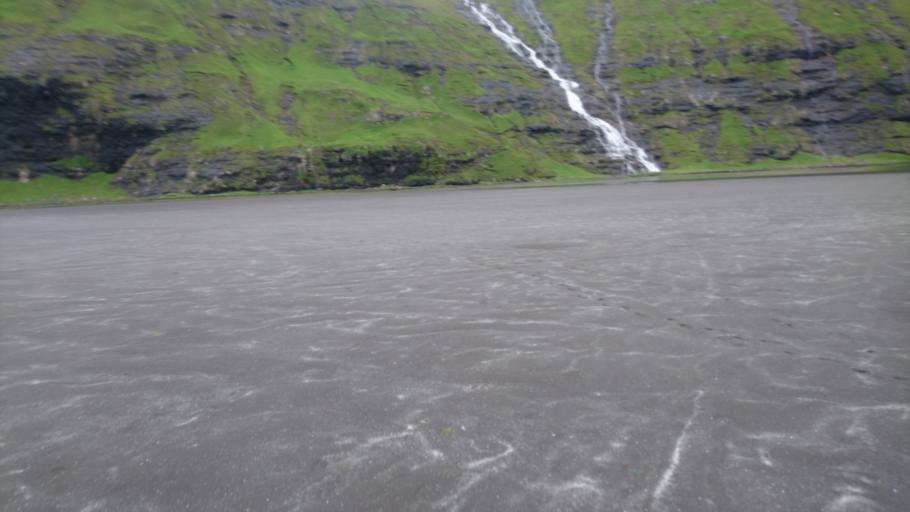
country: FO
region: Streymoy
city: Vestmanna
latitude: 62.2478
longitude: -7.1921
